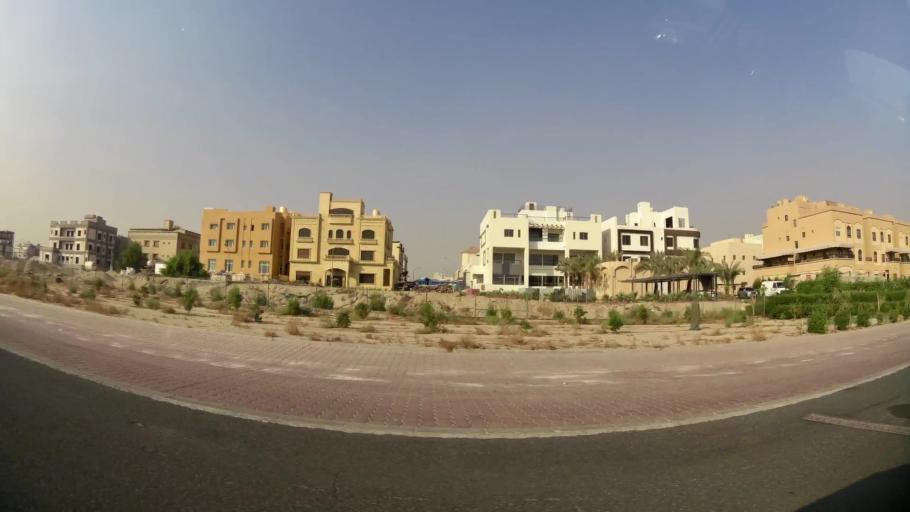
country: KW
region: Al Ahmadi
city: Al Fintas
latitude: 29.1910
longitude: 48.1098
